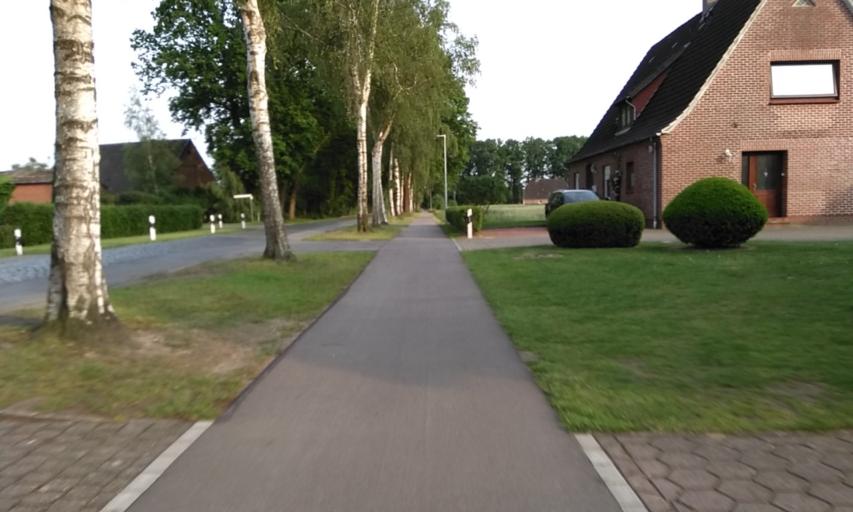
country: DE
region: Lower Saxony
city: Deinste
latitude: 53.5192
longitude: 9.4451
